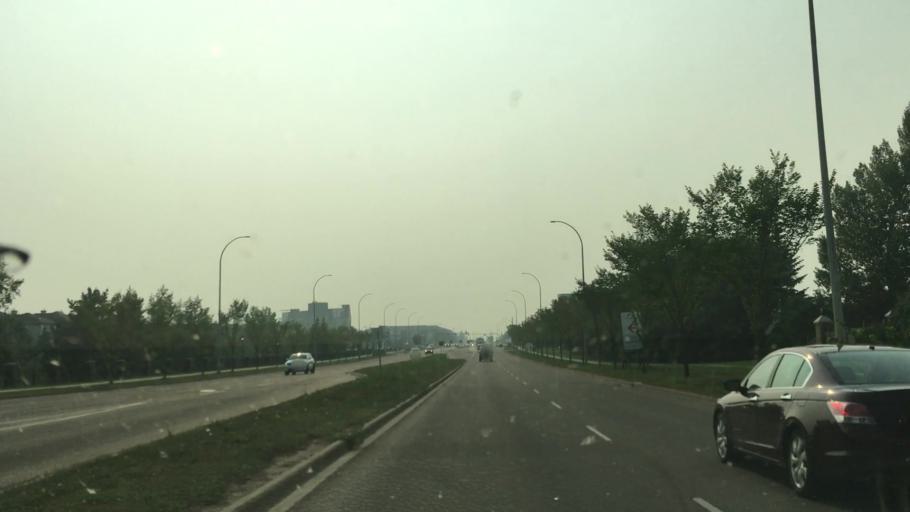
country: CA
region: Alberta
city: Beaumont
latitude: 53.4249
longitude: -113.5099
